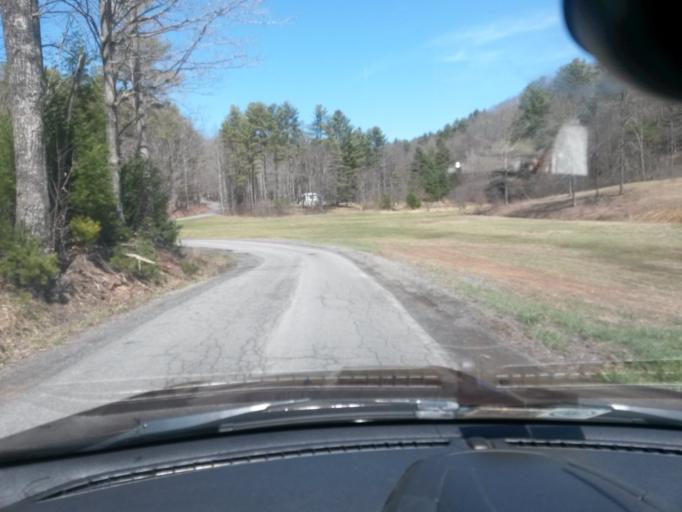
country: US
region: West Virginia
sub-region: Greenbrier County
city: White Sulphur Springs
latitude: 37.6430
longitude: -80.3321
